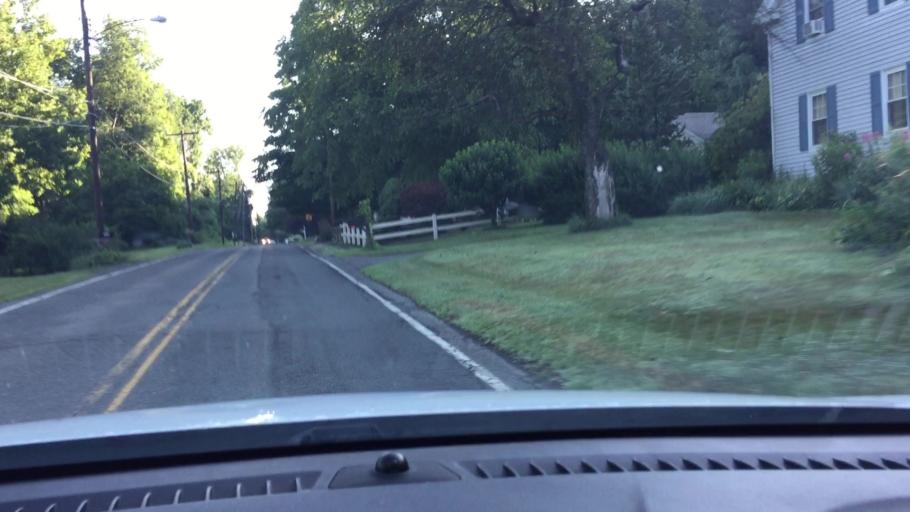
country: US
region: Massachusetts
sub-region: Berkshire County
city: Pittsfield
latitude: 42.4100
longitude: -73.2322
